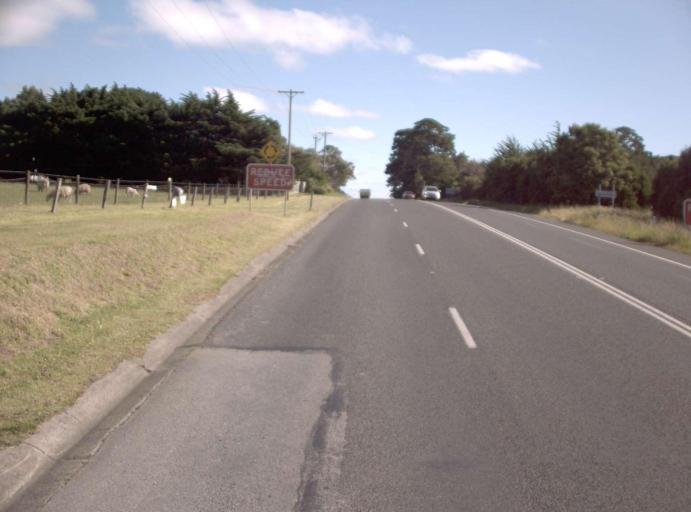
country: AU
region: Victoria
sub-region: Bass Coast
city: North Wonthaggi
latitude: -38.5220
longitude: 145.4476
